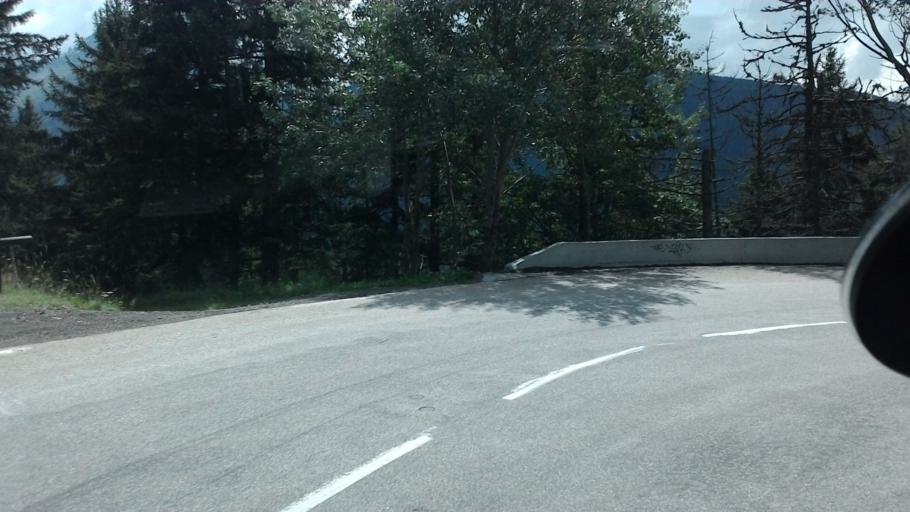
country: FR
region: Rhone-Alpes
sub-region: Departement de la Savoie
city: Seez
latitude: 45.6251
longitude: 6.8320
